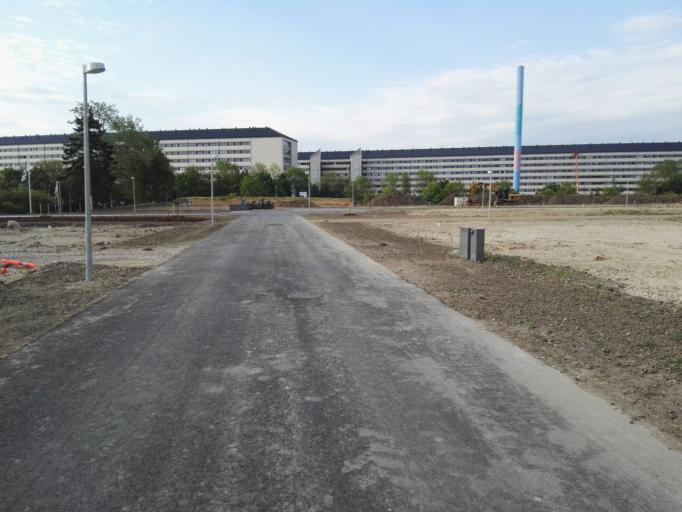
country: DK
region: Capital Region
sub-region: Ballerup Kommune
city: Ballerup
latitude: 55.7300
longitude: 12.3412
